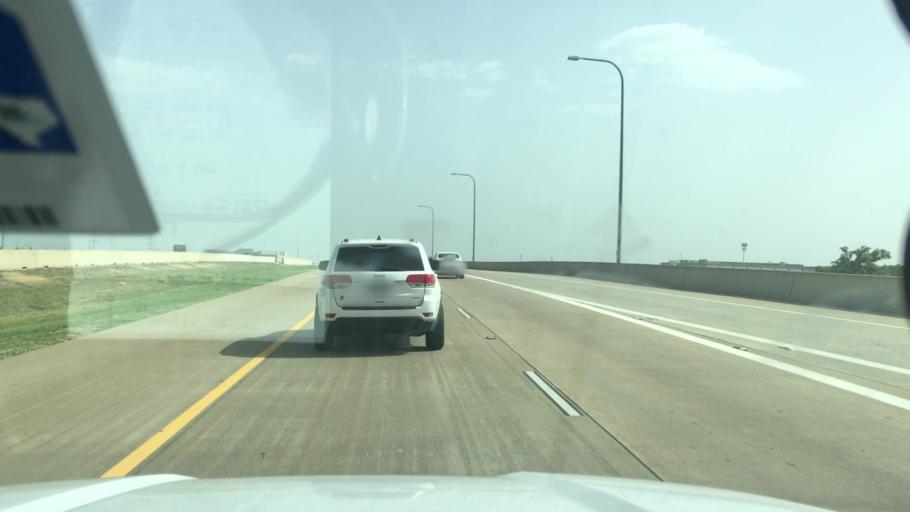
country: US
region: Texas
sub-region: Dallas County
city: Grand Prairie
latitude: 32.7113
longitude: -97.0249
